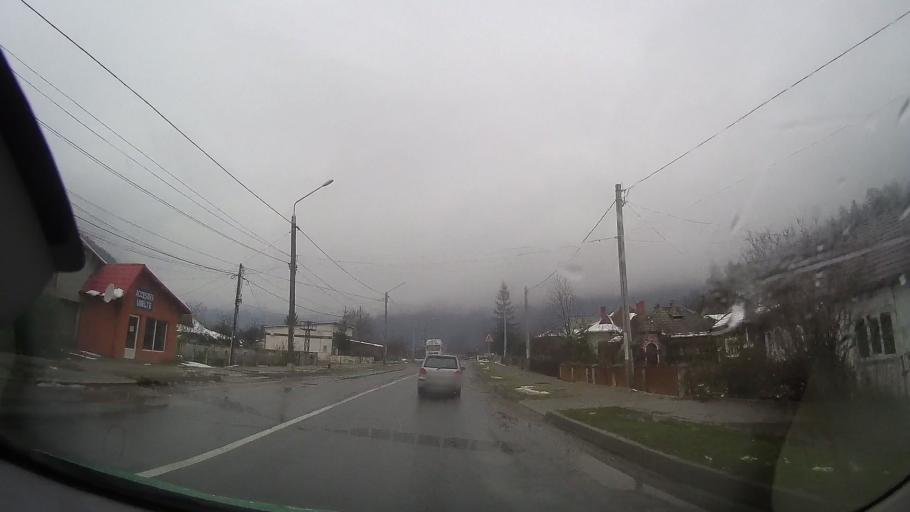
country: RO
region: Neamt
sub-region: Comuna Bicaz
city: Dodeni
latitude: 46.9047
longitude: 26.1092
